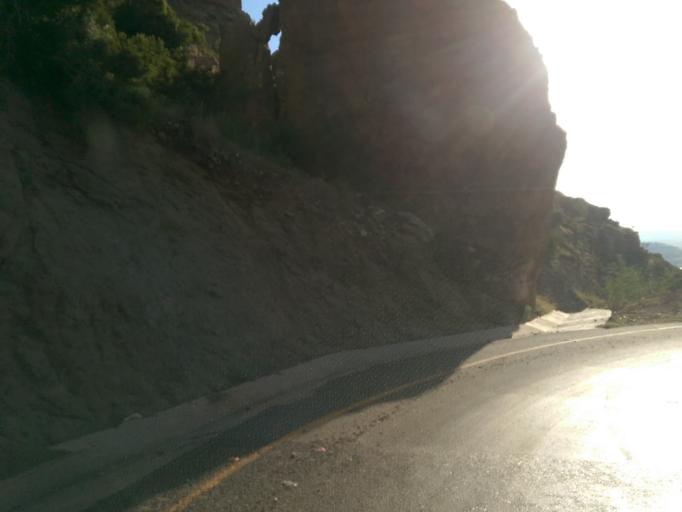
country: LS
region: Maseru
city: Maseru
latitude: -29.3149
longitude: 27.5464
